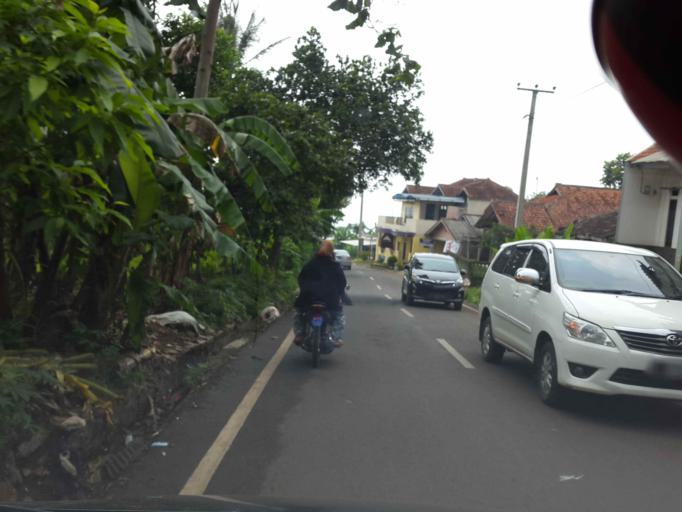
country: ID
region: West Java
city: Padalarang
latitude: -6.8359
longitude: 107.5138
